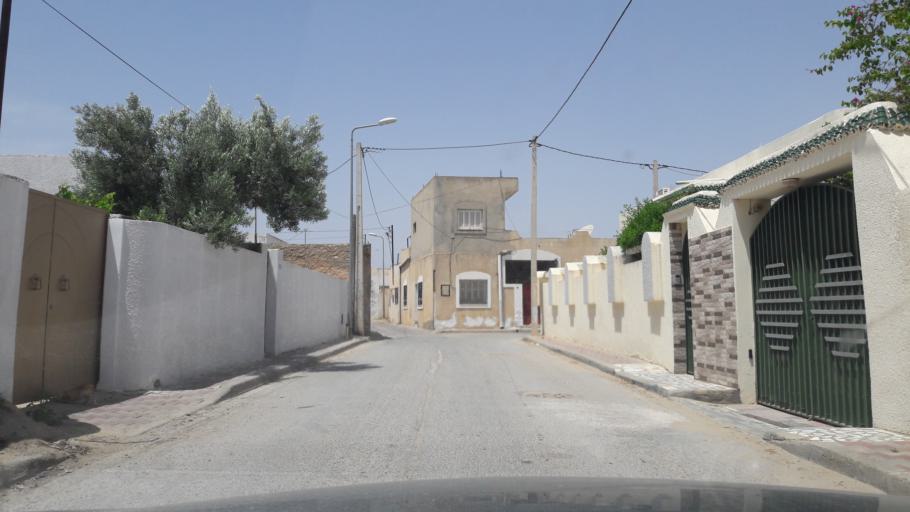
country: TN
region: Safaqis
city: Al Qarmadah
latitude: 34.7786
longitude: 10.7589
